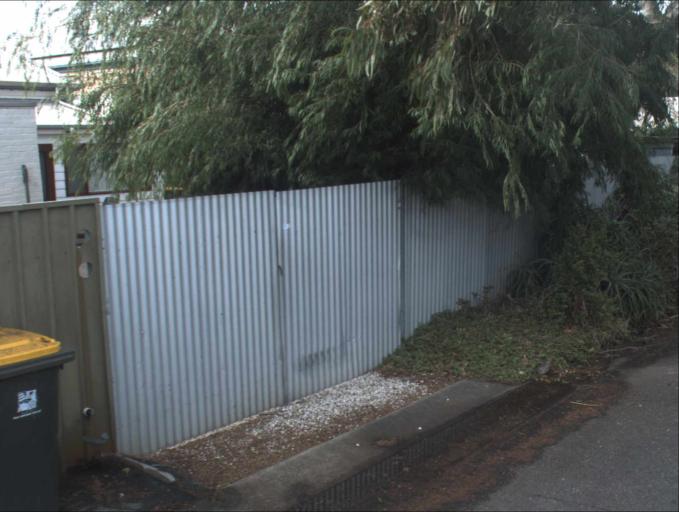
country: AU
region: South Australia
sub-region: Port Adelaide Enfield
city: Birkenhead
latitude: -34.8388
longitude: 138.4913
